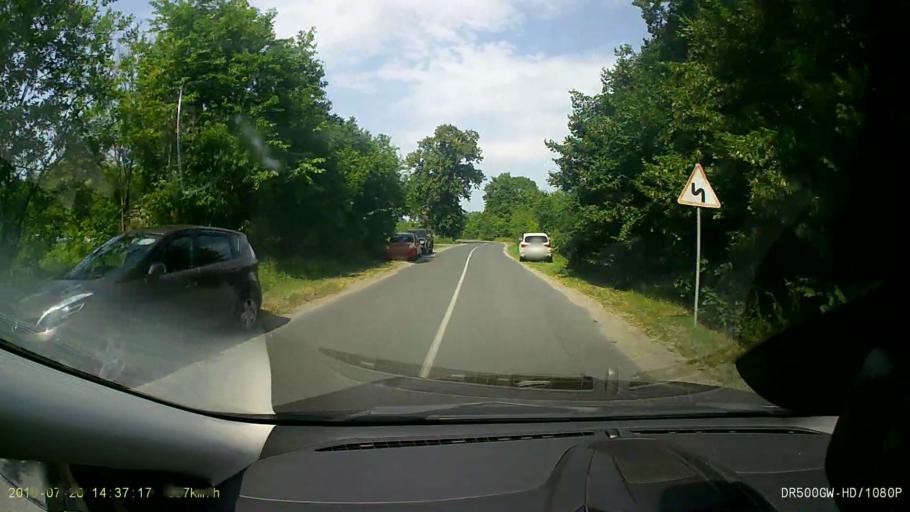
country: RU
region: Kaliningrad
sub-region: Gorod Kaliningrad
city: Yantarnyy
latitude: 54.8676
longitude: 19.9419
